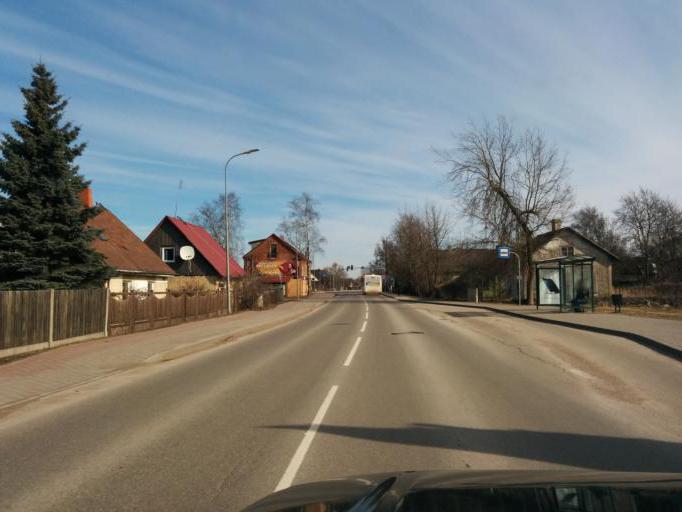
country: LV
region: Jelgava
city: Jelgava
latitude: 56.6353
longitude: 23.7075
